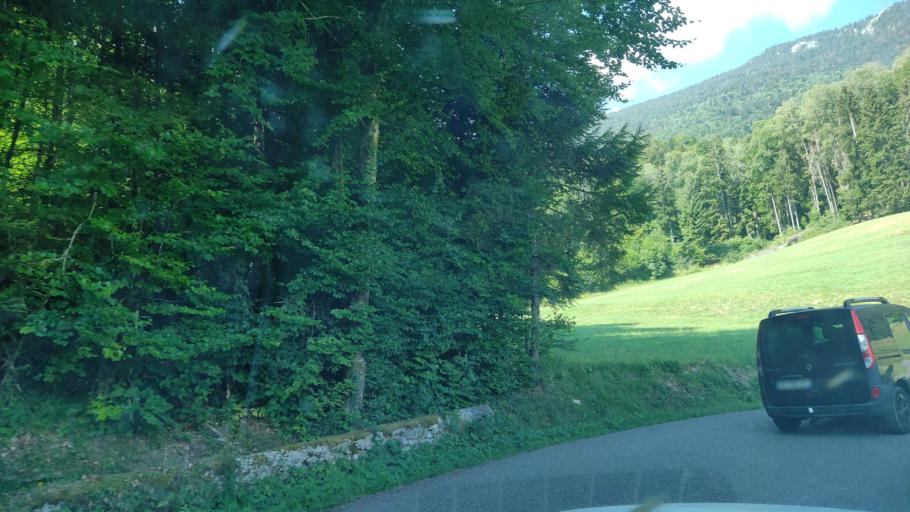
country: FR
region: Rhone-Alpes
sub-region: Departement de la Haute-Savoie
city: Saint-Jorioz
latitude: 45.8075
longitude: 6.1392
